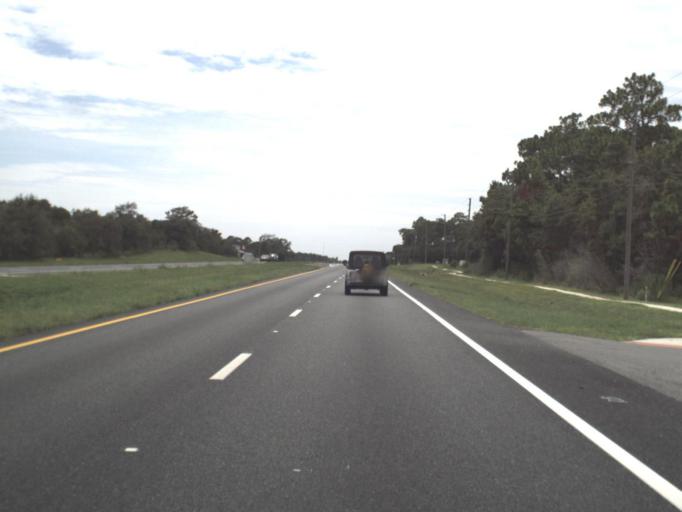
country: US
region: Florida
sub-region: Citrus County
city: Citrus Hills
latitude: 28.8580
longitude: -82.4311
